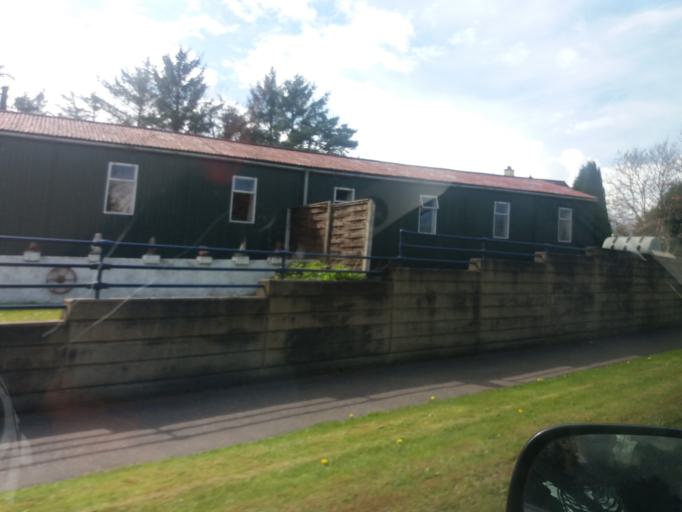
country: GB
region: Northern Ireland
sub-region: Fermanagh District
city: Enniskillen
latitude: 54.3561
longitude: -7.6680
